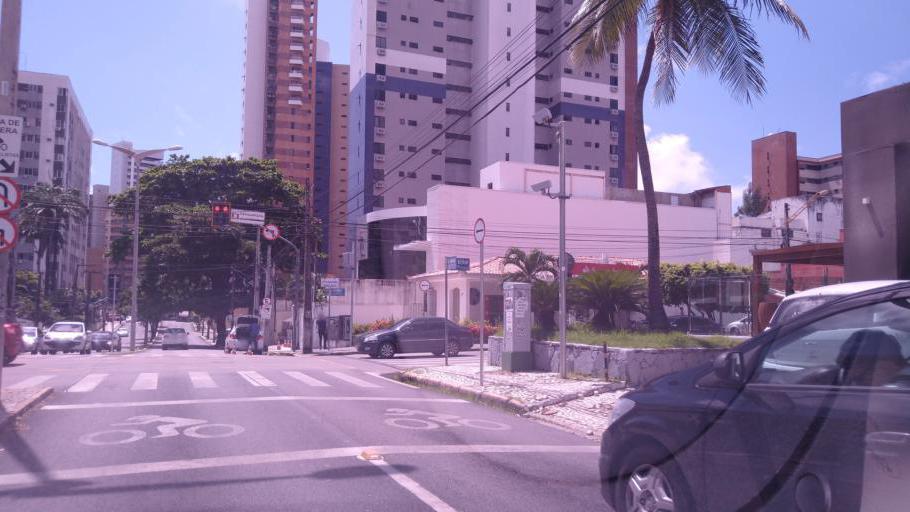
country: BR
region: Ceara
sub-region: Fortaleza
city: Fortaleza
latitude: -3.7311
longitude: -38.4913
